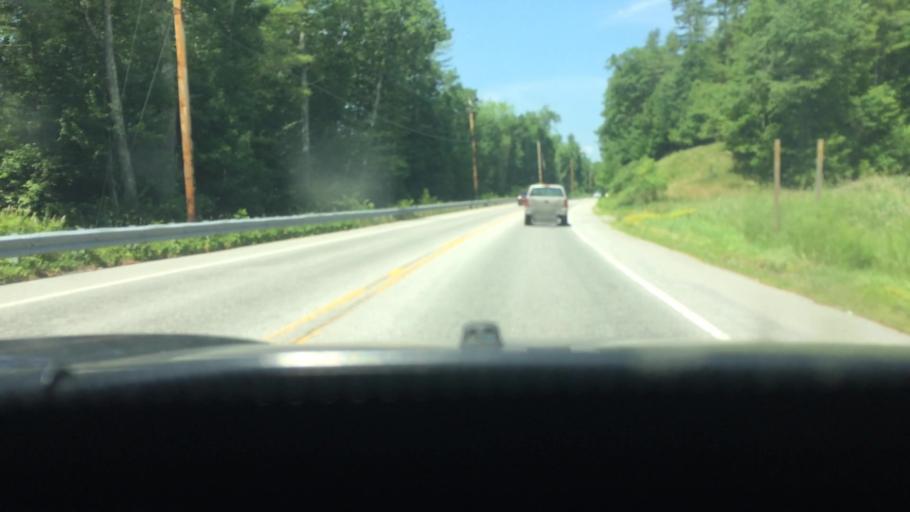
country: US
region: Maine
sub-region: Androscoggin County
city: Minot
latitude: 44.0828
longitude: -70.3117
